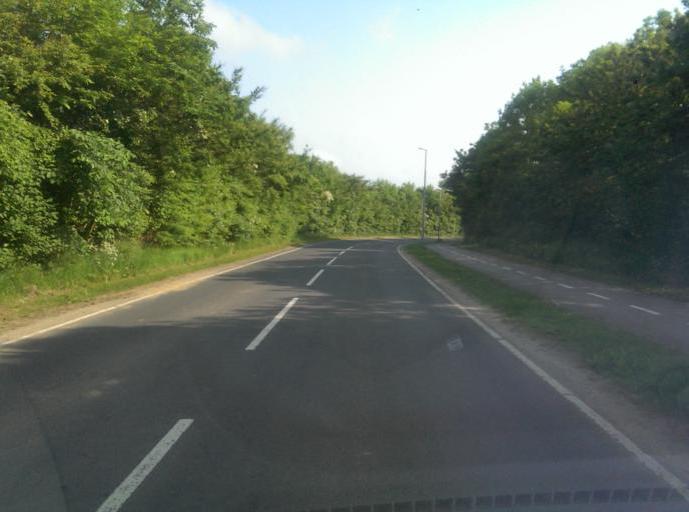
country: DK
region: South Denmark
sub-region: Esbjerg Kommune
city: Bramming
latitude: 55.4246
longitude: 8.6517
